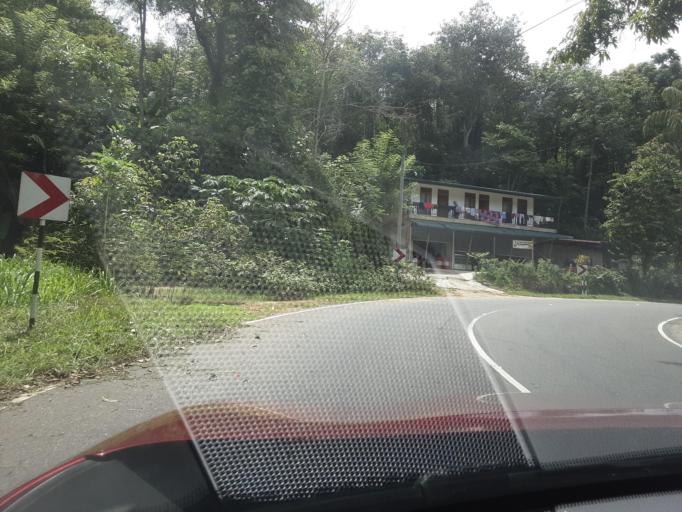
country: LK
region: Uva
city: Monaragala
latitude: 6.8964
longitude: 81.2735
